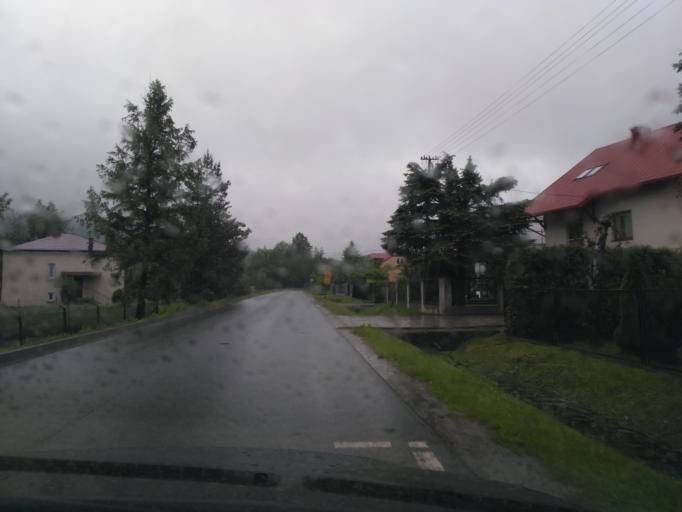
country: PL
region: Lesser Poland Voivodeship
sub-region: Powiat gorlicki
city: Lipinki
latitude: 49.6434
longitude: 21.2917
